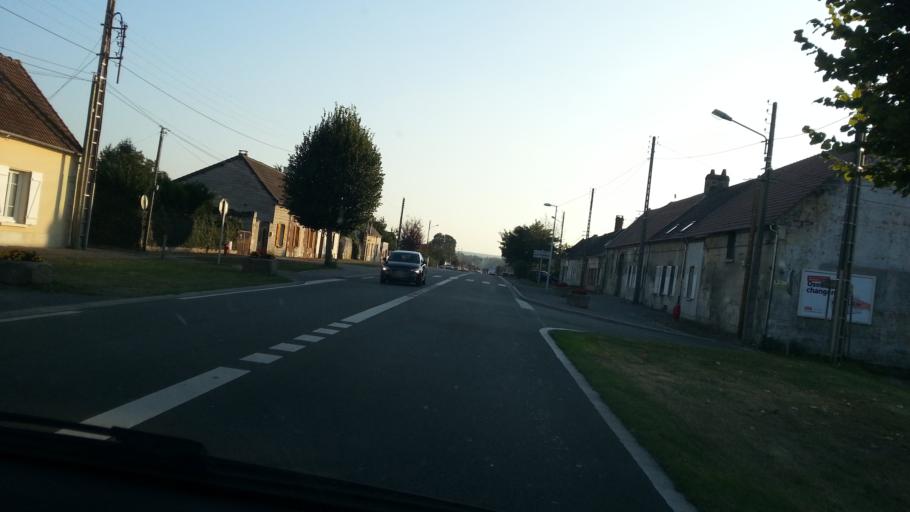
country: FR
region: Picardie
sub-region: Departement de l'Oise
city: Saint-Martin-Longueau
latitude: 49.3452
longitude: 2.6073
